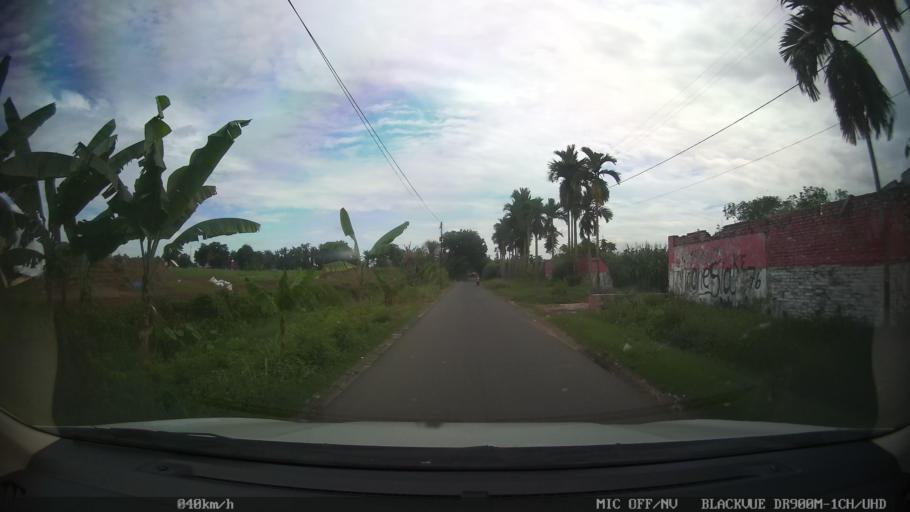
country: ID
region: North Sumatra
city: Sunggal
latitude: 3.5855
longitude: 98.5653
